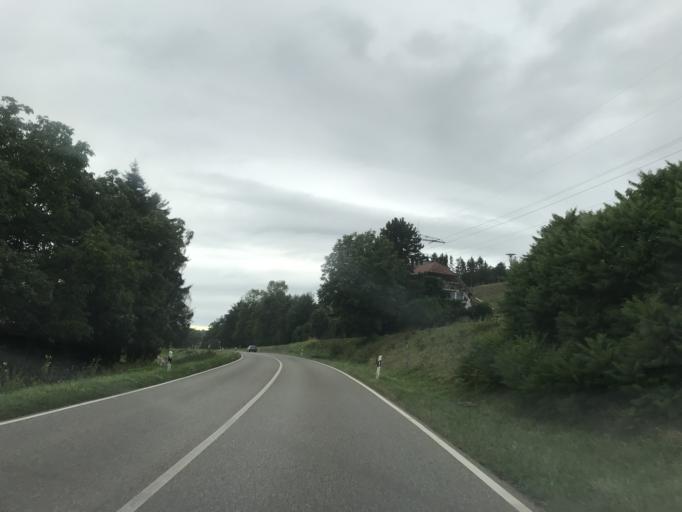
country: DE
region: Baden-Wuerttemberg
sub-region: Freiburg Region
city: Murg
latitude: 47.5582
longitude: 7.9999
